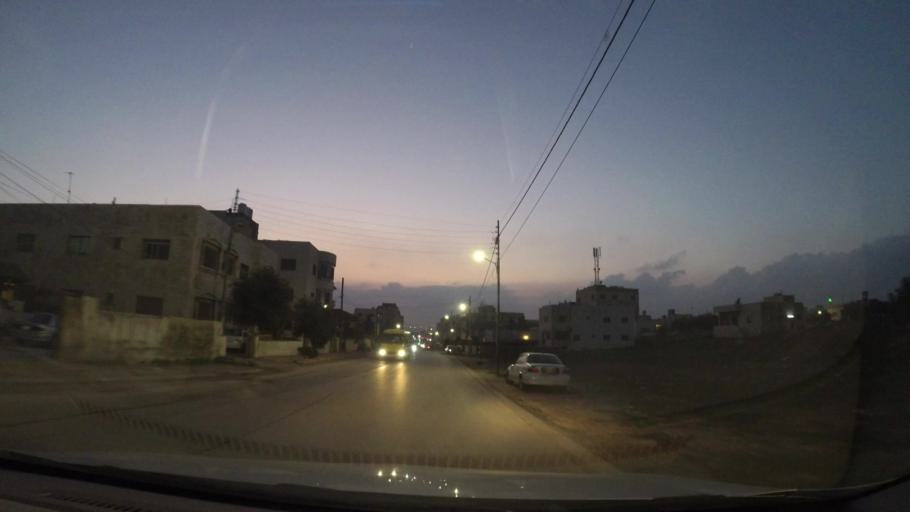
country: JO
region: Amman
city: Al Bunayyat ash Shamaliyah
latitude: 31.8945
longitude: 35.9221
